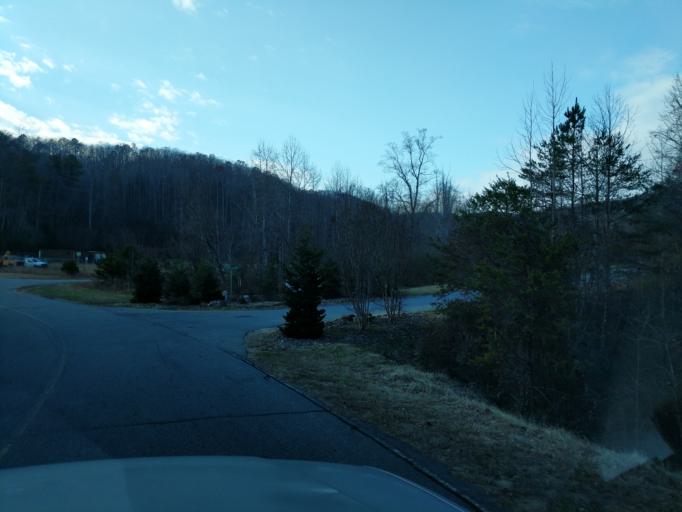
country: US
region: North Carolina
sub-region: McDowell County
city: West Marion
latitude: 35.6432
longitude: -81.9895
